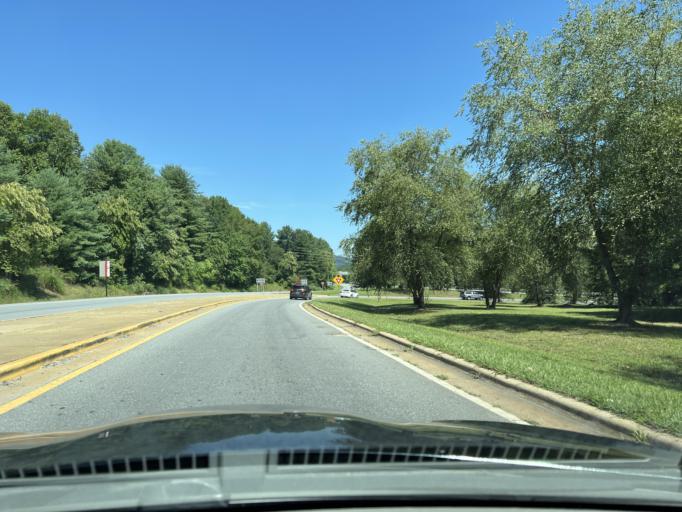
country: US
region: North Carolina
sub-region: Buncombe County
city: Biltmore Forest
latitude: 35.5675
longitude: -82.5093
